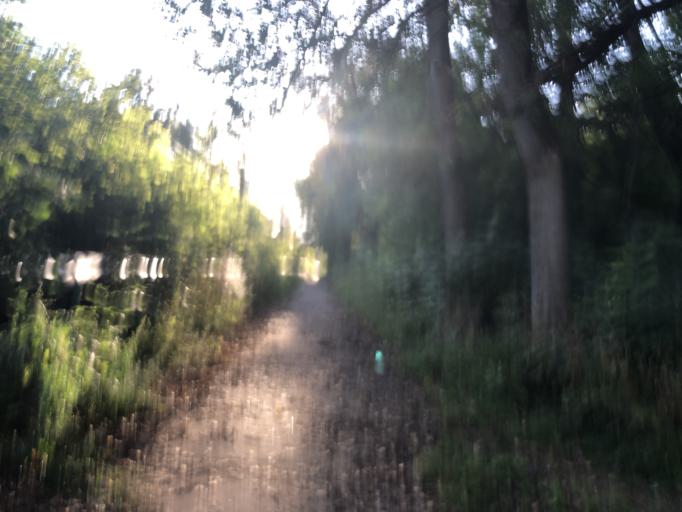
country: RU
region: Tverskaya
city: Rzhev
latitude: 56.2436
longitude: 34.3300
